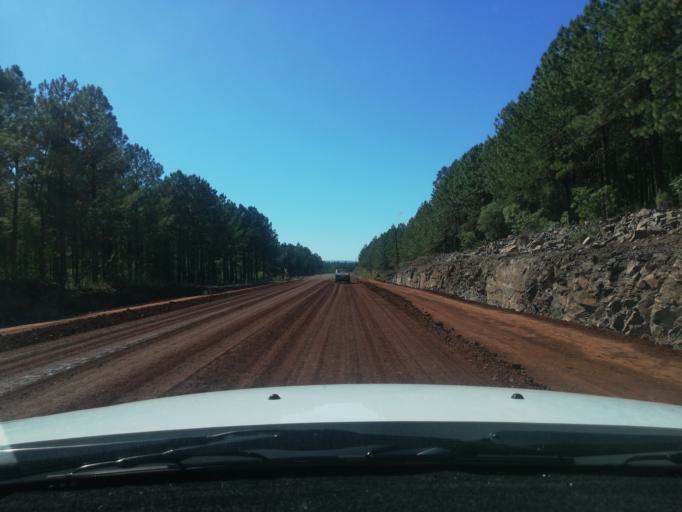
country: AR
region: Misiones
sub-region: Departamento de Candelaria
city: Candelaria
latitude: -27.5189
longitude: -55.7279
